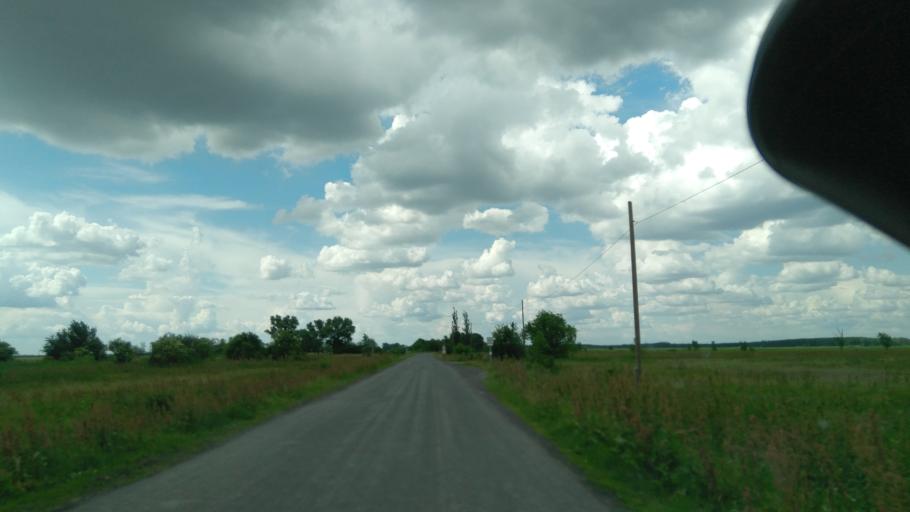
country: HU
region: Bekes
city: Szeghalom
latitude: 47.1200
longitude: 21.0879
